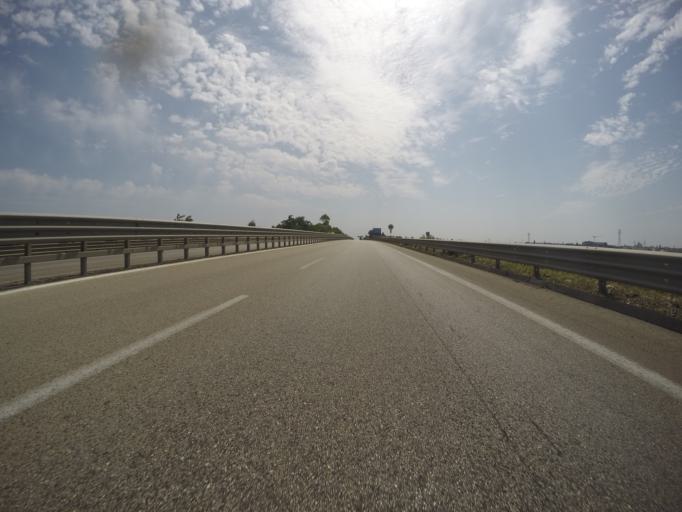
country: IT
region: Apulia
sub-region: Provincia di Brindisi
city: Francavilla Fontana
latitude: 40.5465
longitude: 17.5677
